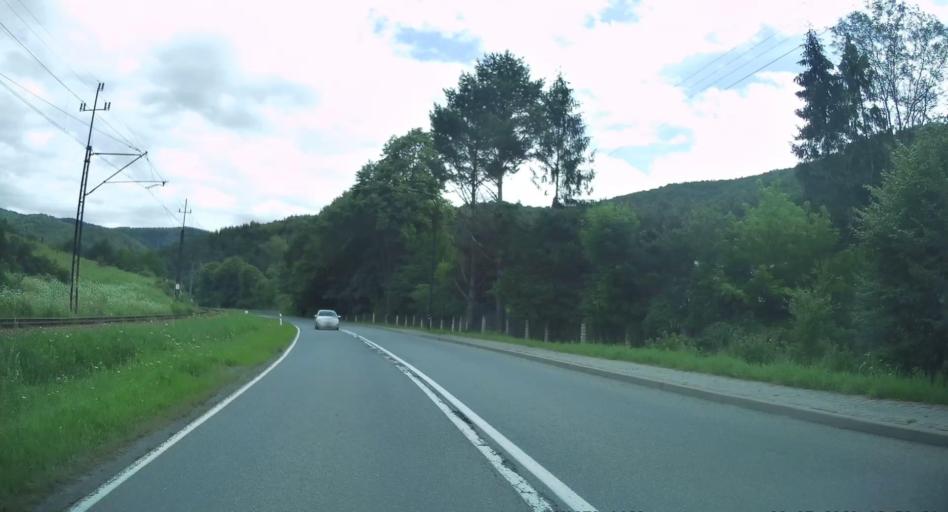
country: PL
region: Lesser Poland Voivodeship
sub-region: Powiat nowosadecki
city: Piwniczna-Zdroj
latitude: 49.3617
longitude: 20.7859
